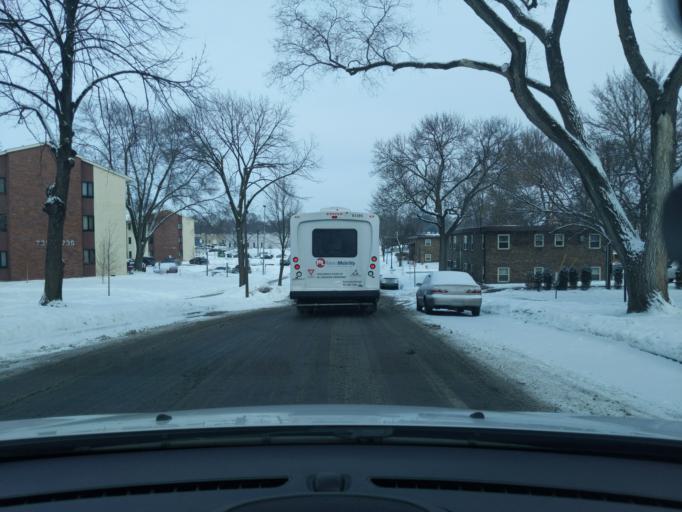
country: US
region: Minnesota
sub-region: Ramsey County
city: Falcon Heights
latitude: 44.9632
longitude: -93.1366
